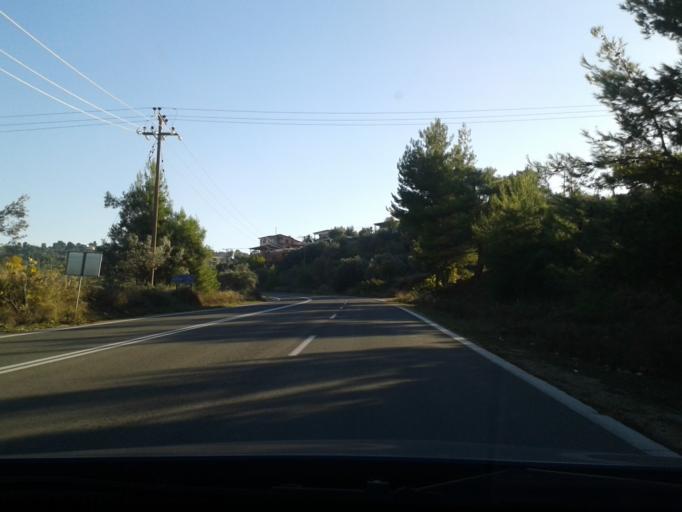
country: GR
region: Attica
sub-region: Nomarchia Anatolikis Attikis
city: Markopoulo Oropou
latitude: 38.2924
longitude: 23.8186
